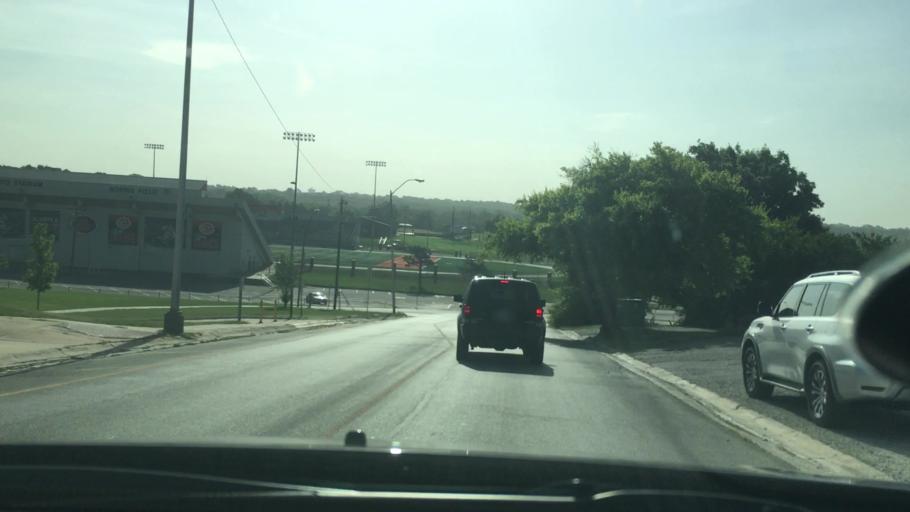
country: US
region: Oklahoma
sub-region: Pontotoc County
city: Ada
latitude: 34.7714
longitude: -96.6623
